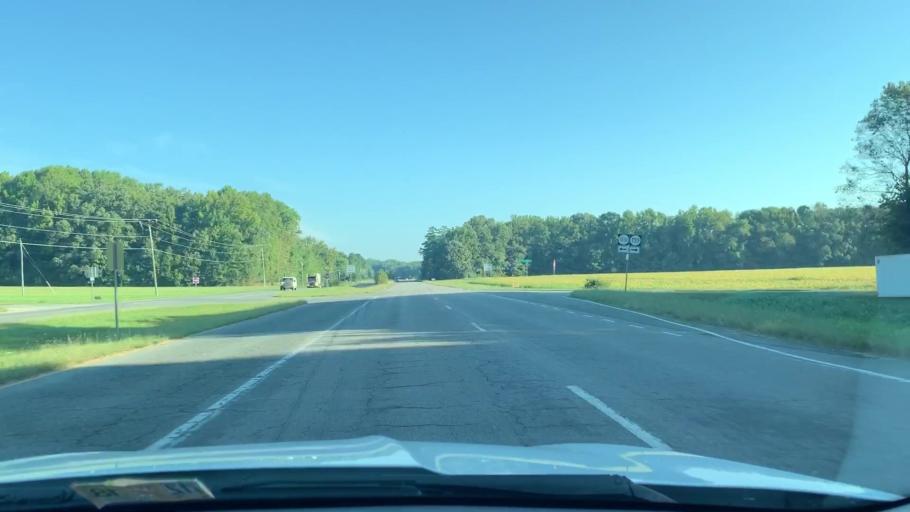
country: US
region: Virginia
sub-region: Lancaster County
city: Kilmarnock
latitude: 37.6874
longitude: -76.3764
